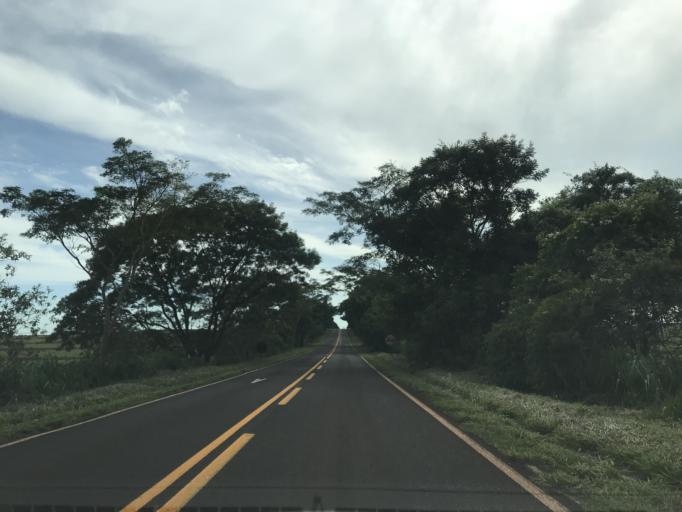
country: BR
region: Parana
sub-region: Terra Rica
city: Terra Rica
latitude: -22.7745
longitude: -52.6522
